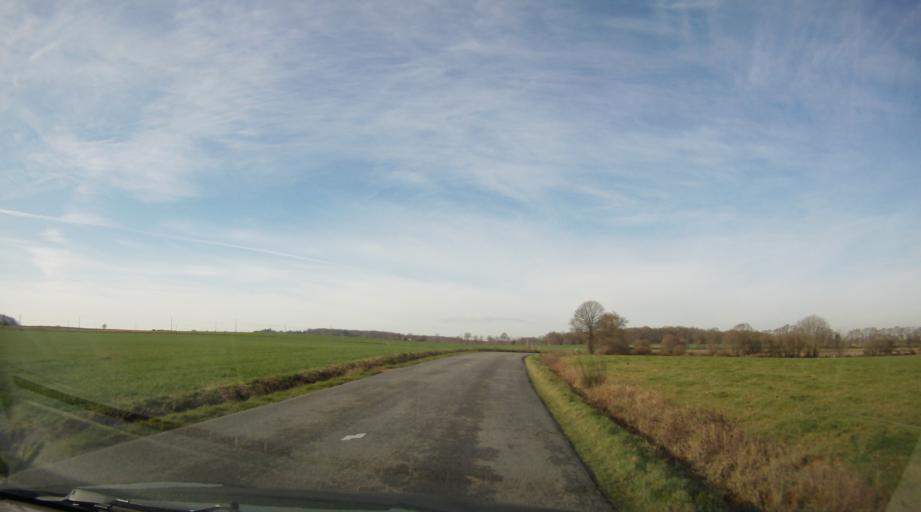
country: FR
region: Brittany
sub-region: Departement d'Ille-et-Vilaine
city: Bourgbarre
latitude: 47.9943
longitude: -1.6349
